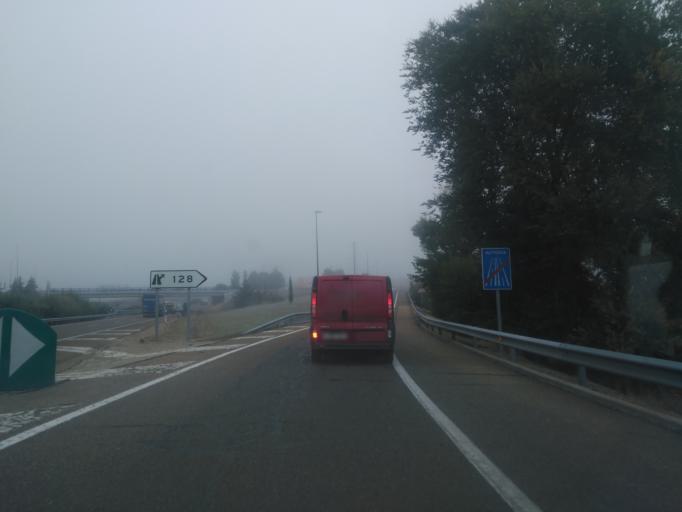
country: ES
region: Castille and Leon
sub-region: Provincia de Valladolid
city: Zaratan
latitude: 41.6330
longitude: -4.7766
